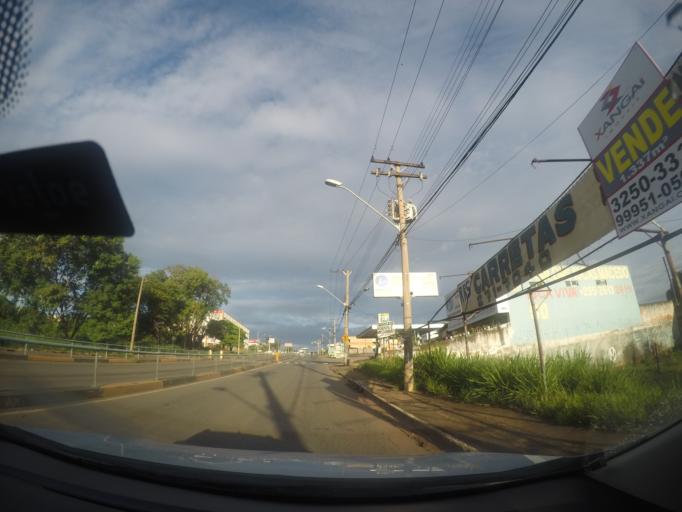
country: BR
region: Goias
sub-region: Goiania
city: Goiania
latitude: -16.6649
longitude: -49.3174
